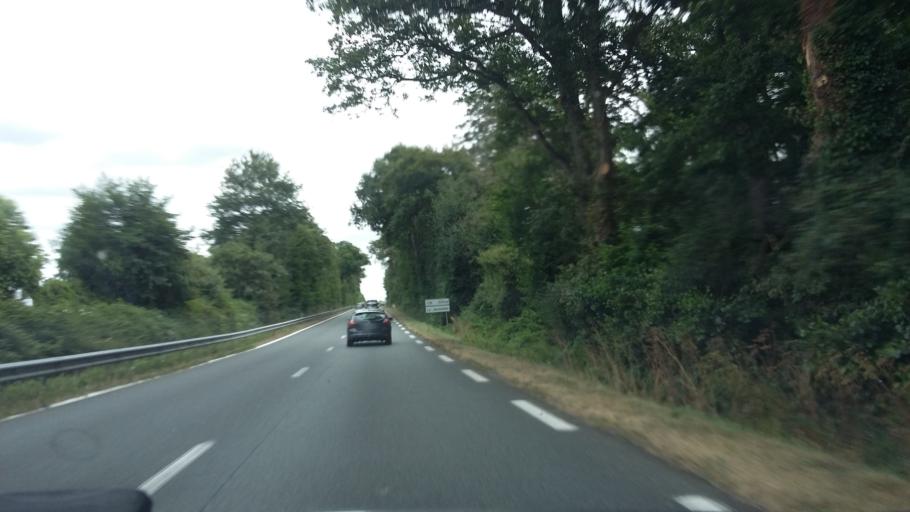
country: FR
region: Pays de la Loire
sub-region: Departement de la Vendee
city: Mouilleron-le-Captif
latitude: 46.6939
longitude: -1.4765
